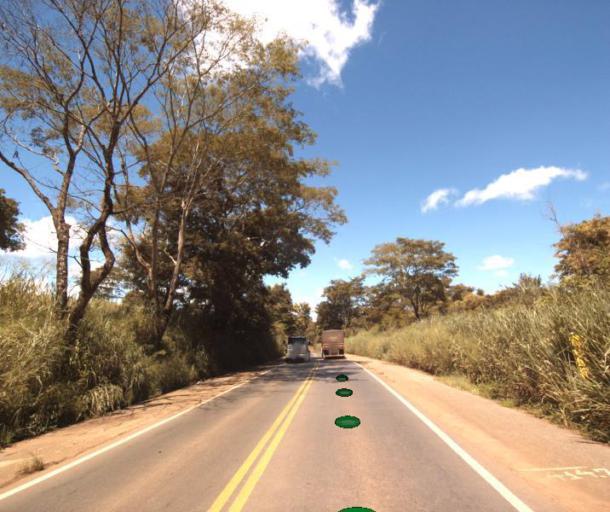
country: BR
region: Goias
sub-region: Anapolis
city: Anapolis
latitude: -16.1355
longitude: -49.0480
